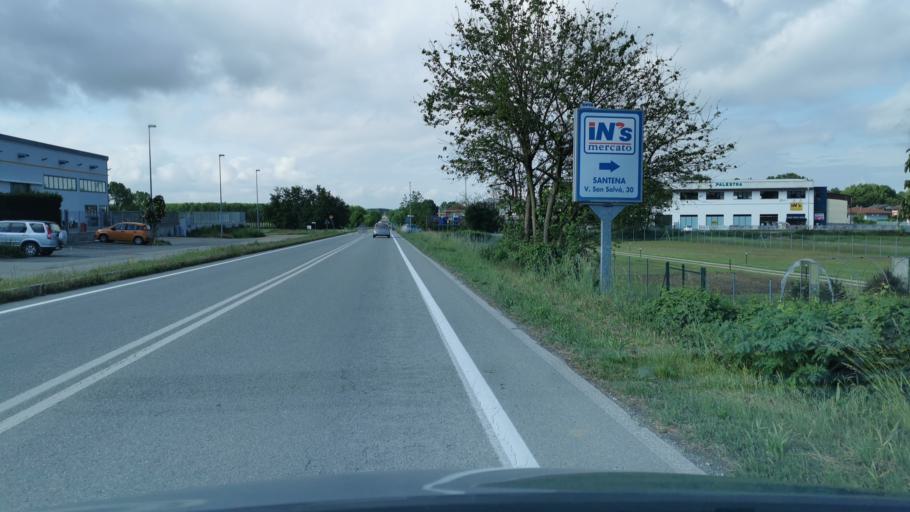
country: IT
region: Piedmont
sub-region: Provincia di Torino
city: Santena
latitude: 44.9532
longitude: 7.7859
